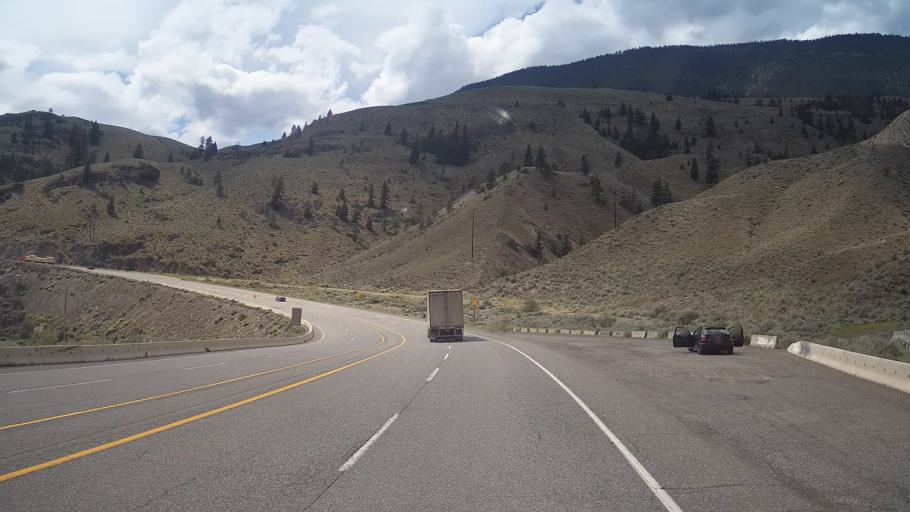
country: CA
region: British Columbia
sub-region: Thompson-Nicola Regional District
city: Ashcroft
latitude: 50.5100
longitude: -121.2846
